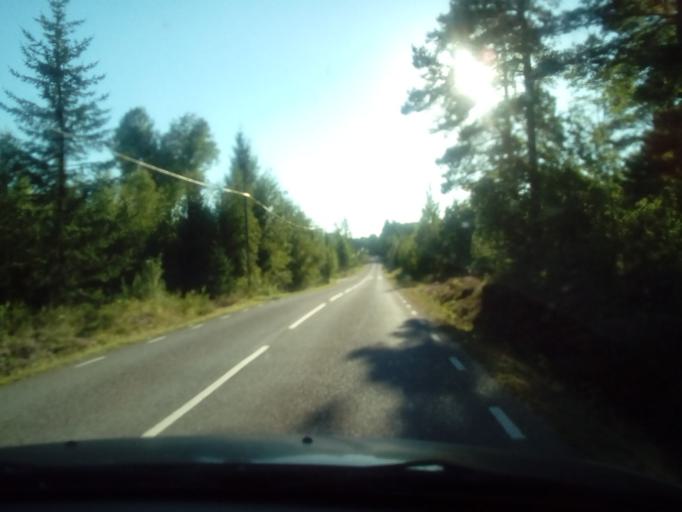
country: SE
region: Kalmar
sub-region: Vasterviks Kommun
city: Ankarsrum
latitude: 57.7890
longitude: 16.3167
